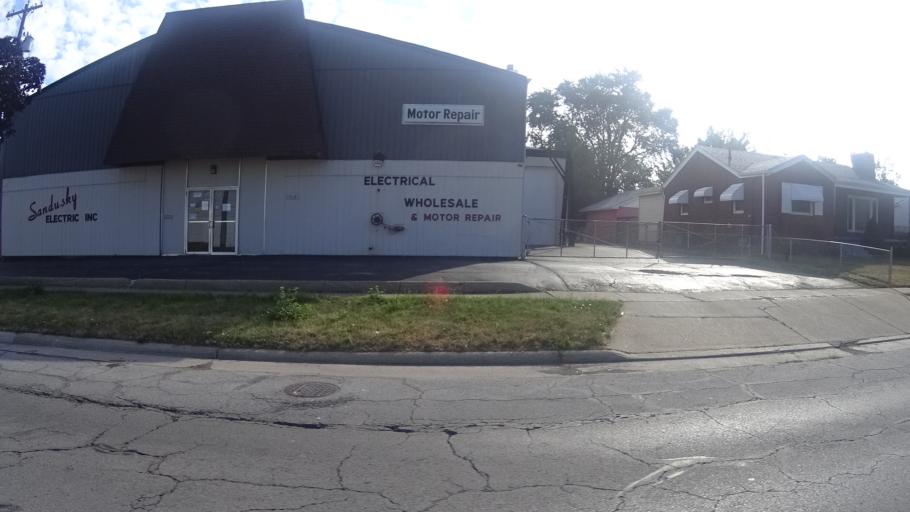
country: US
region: Ohio
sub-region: Erie County
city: Sandusky
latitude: 41.4441
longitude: -82.6993
